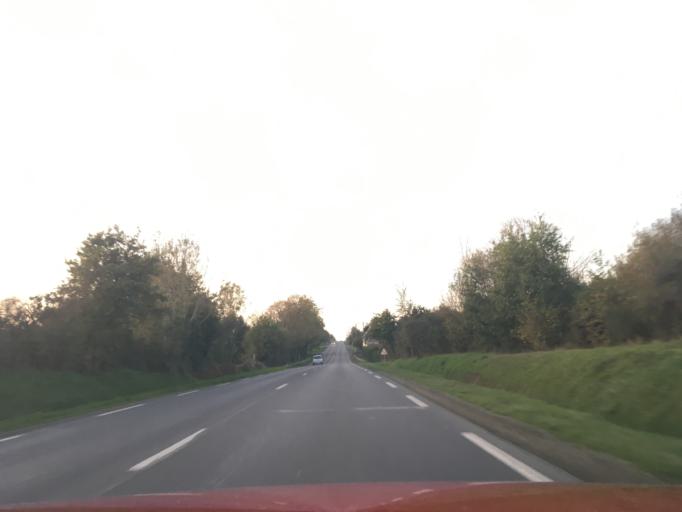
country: FR
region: Lower Normandy
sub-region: Departement de la Manche
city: Saint-Planchers
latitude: 48.8002
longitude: -1.5238
